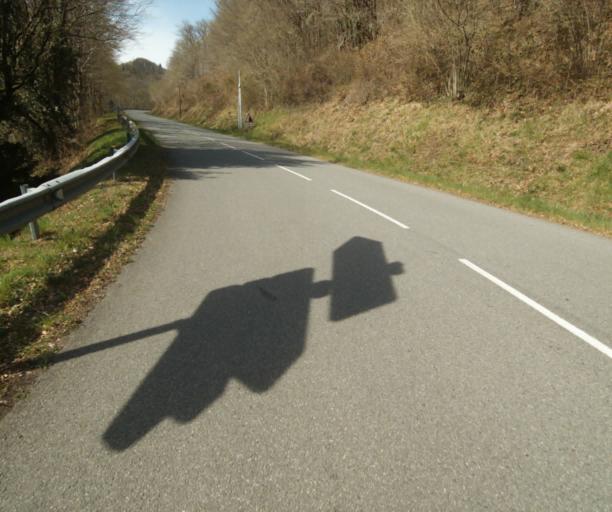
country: FR
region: Limousin
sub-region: Departement de la Correze
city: Naves
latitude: 45.3383
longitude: 1.7921
